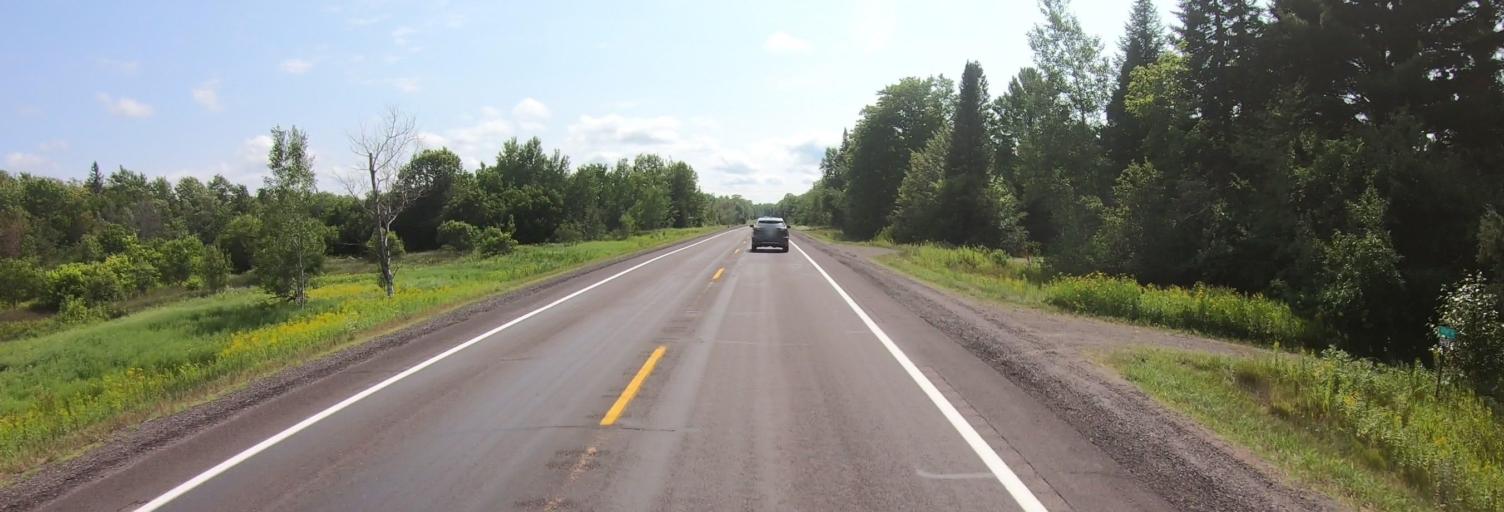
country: US
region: Michigan
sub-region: Houghton County
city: Hancock
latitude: 46.8805
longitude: -88.8671
